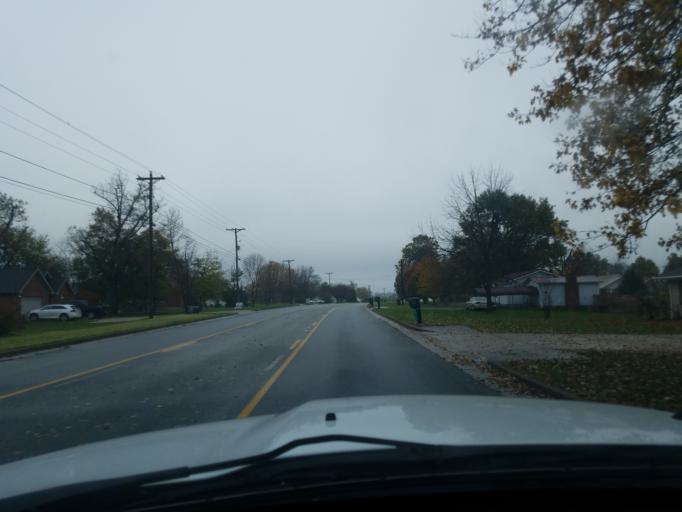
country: US
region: Kentucky
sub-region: Larue County
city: Hodgenville
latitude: 37.5532
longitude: -85.7131
